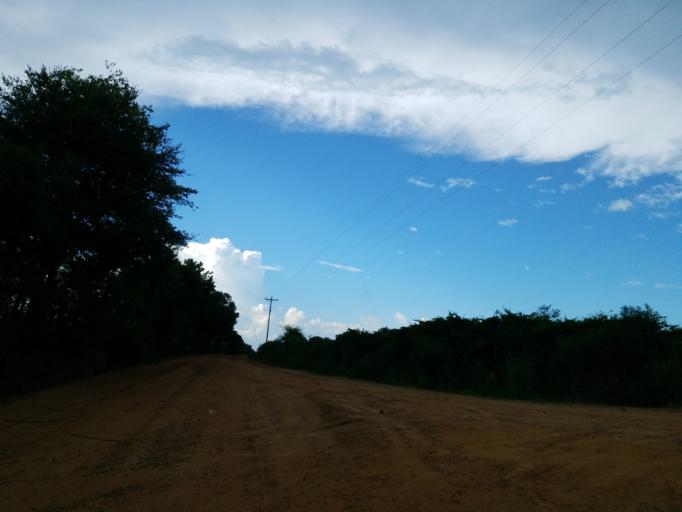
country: US
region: Georgia
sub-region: Tift County
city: Omega
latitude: 31.2756
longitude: -83.5275
